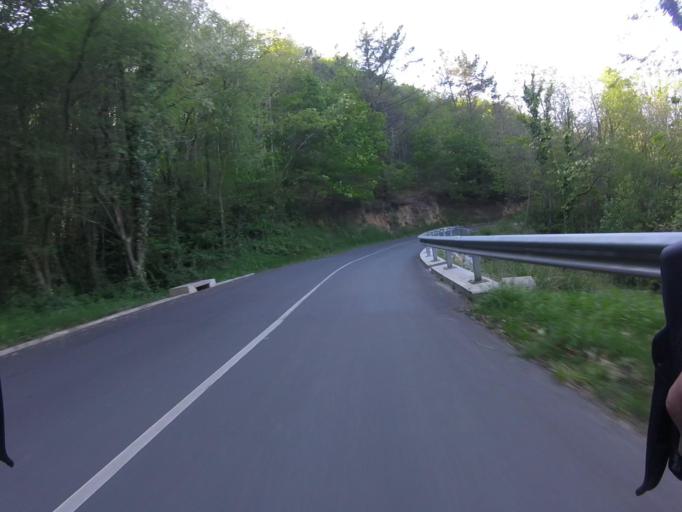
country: ES
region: Basque Country
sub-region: Provincia de Guipuzcoa
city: Fuenterrabia
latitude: 43.3674
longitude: -1.8273
